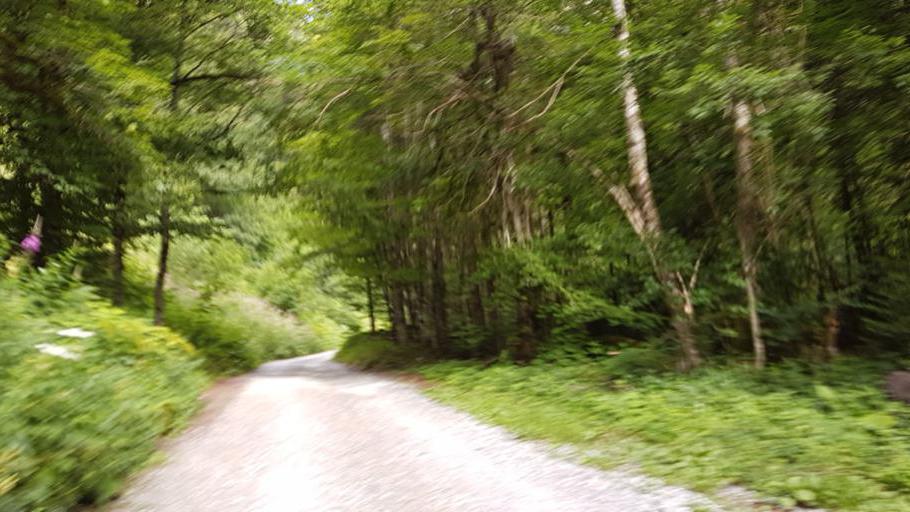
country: CH
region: Bern
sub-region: Obersimmental-Saanen District
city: Boltigen
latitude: 46.6736
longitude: 7.4555
